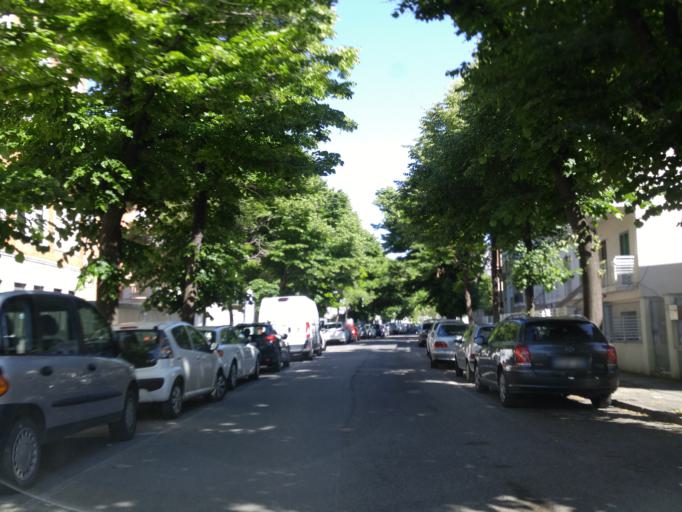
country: IT
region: The Marches
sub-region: Provincia di Pesaro e Urbino
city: Pesaro
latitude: 43.9198
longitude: 12.9074
